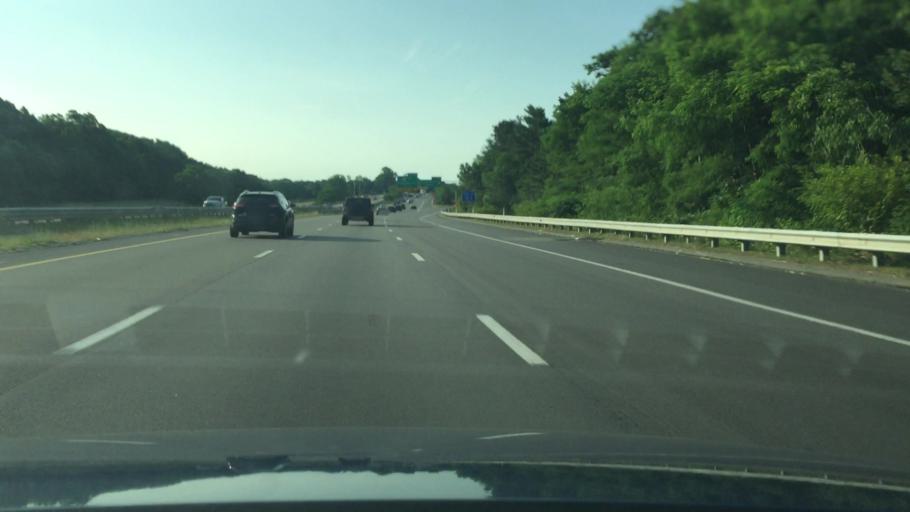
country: US
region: Massachusetts
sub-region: Plymouth County
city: North Plymouth
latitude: 41.9584
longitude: -70.6866
